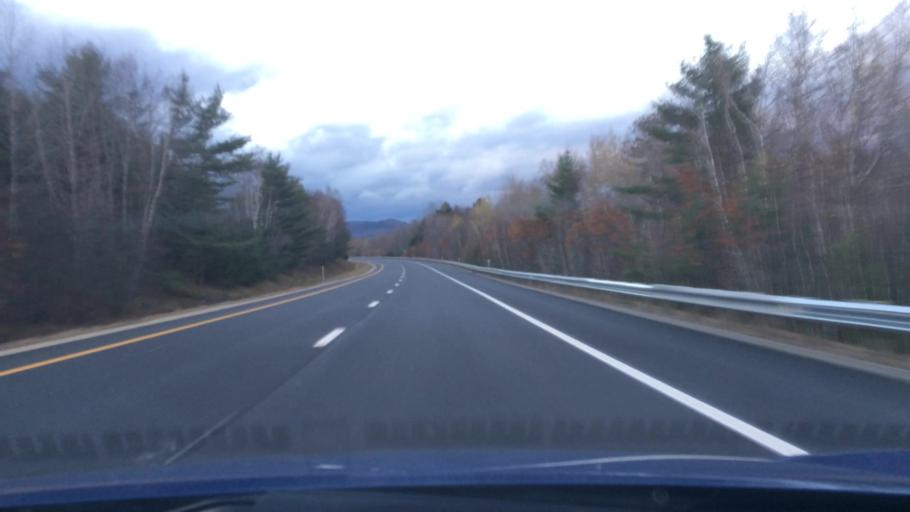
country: US
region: New Hampshire
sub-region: Grafton County
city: Thornton
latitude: 43.8912
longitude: -71.6824
